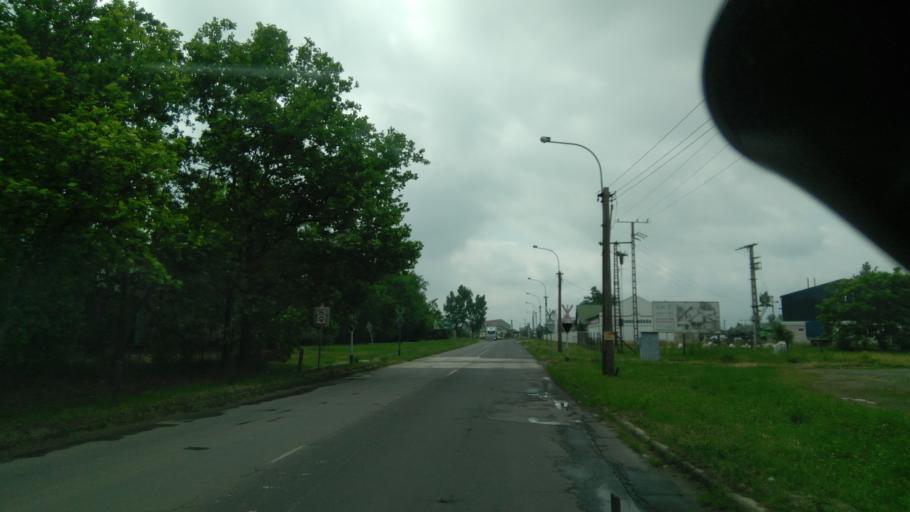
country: HU
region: Bekes
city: Bekescsaba
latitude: 46.6615
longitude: 21.0896
